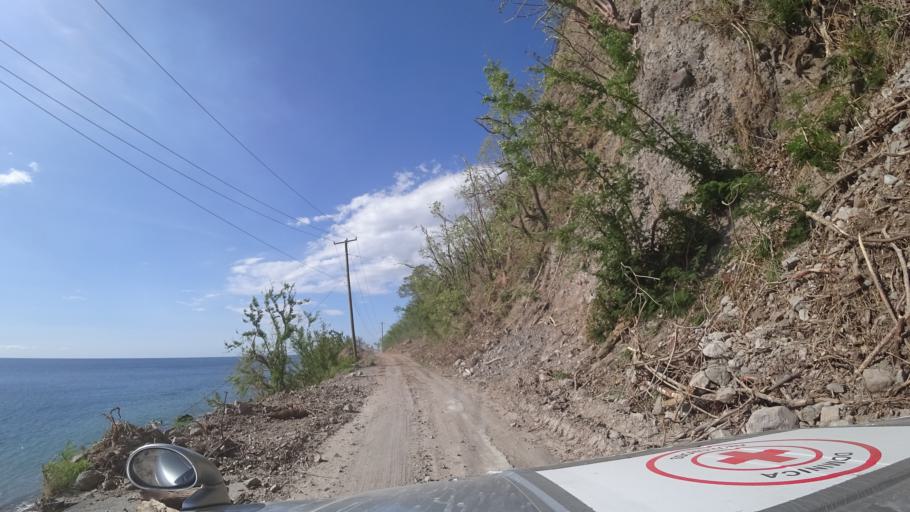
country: DM
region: Saint Luke
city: Pointe Michel
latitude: 15.2488
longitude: -61.3739
